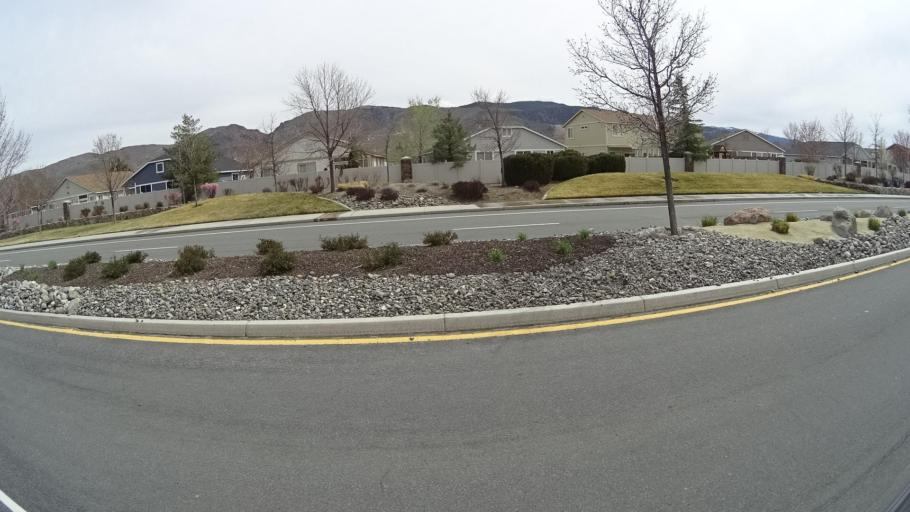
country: US
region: Nevada
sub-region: Washoe County
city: Sparks
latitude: 39.4284
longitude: -119.7256
